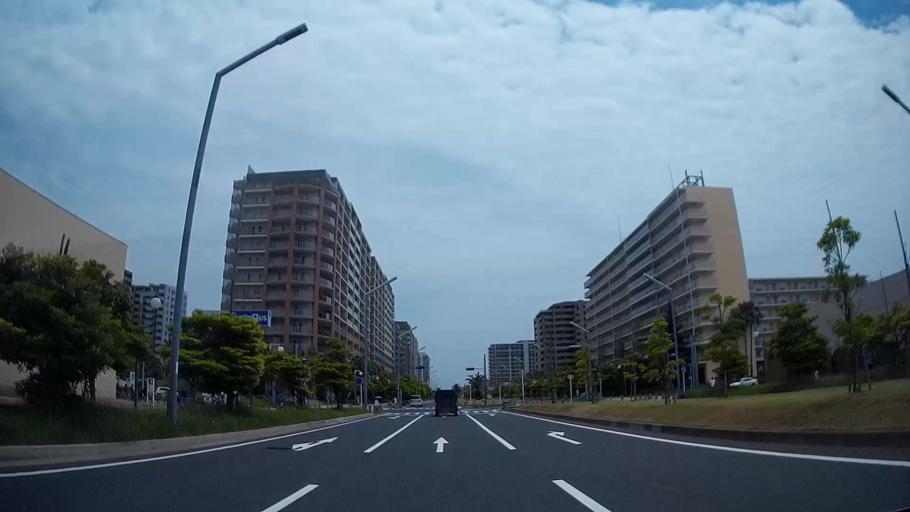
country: JP
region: Tokyo
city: Urayasu
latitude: 35.6422
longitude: 139.9254
